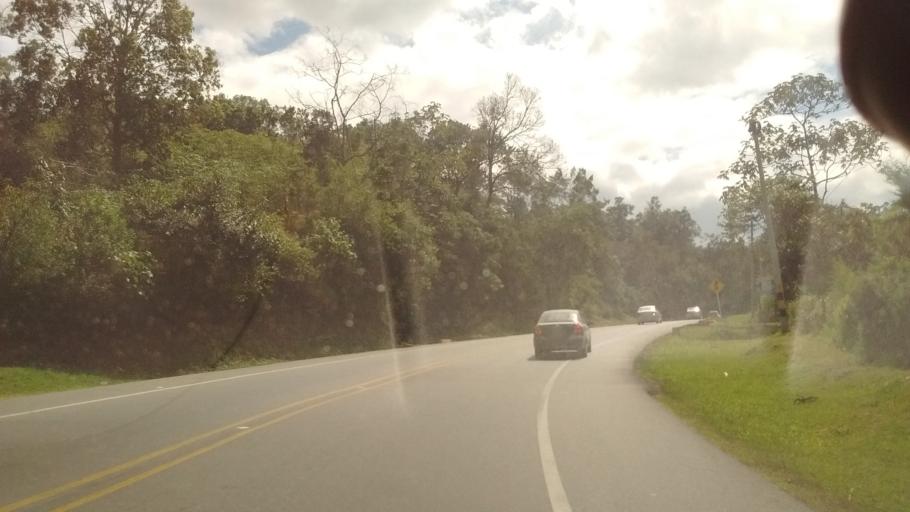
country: CO
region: Cauca
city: Cajibio
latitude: 2.6094
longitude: -76.5281
